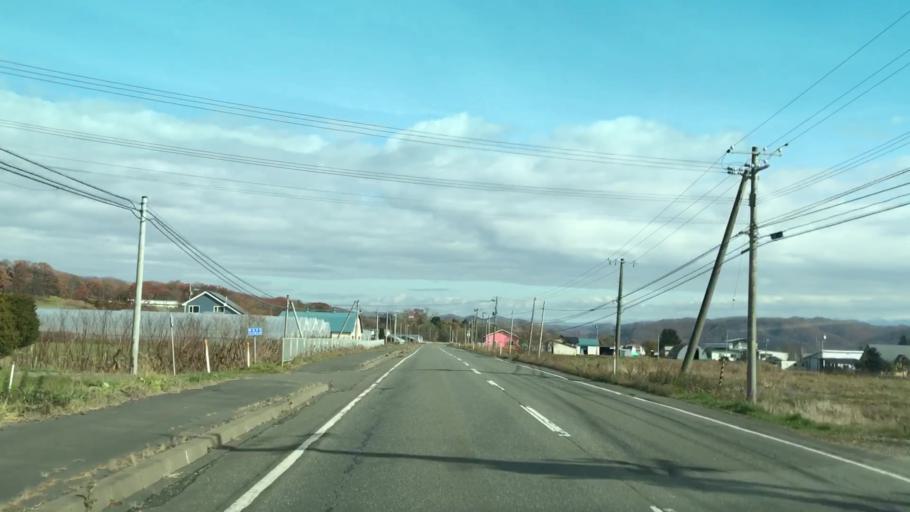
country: JP
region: Hokkaido
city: Shizunai-furukawacho
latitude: 42.5735
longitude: 142.1040
